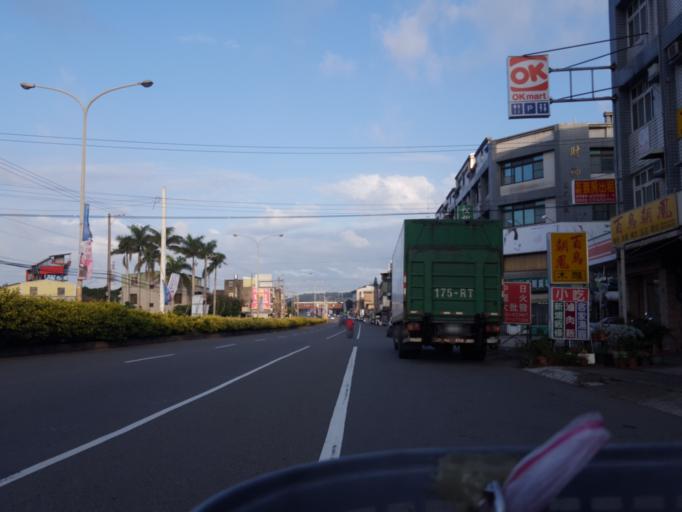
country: TW
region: Taiwan
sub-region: Hsinchu
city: Zhubei
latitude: 24.8782
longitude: 121.0564
